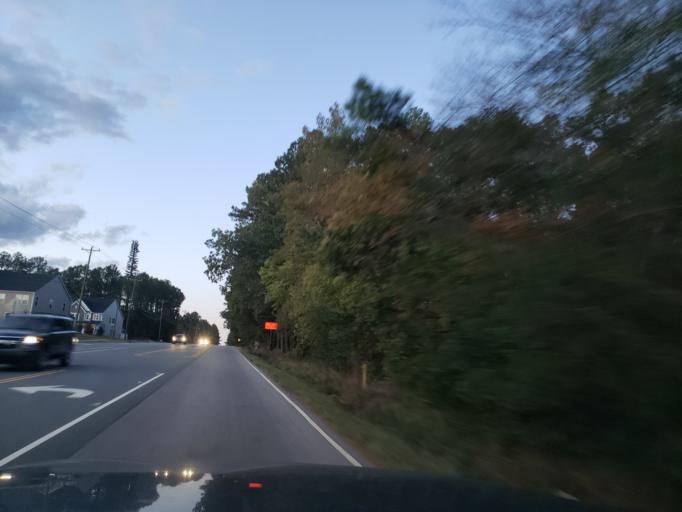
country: US
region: North Carolina
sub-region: Orange County
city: Chapel Hill
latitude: 35.8904
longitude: -78.9576
